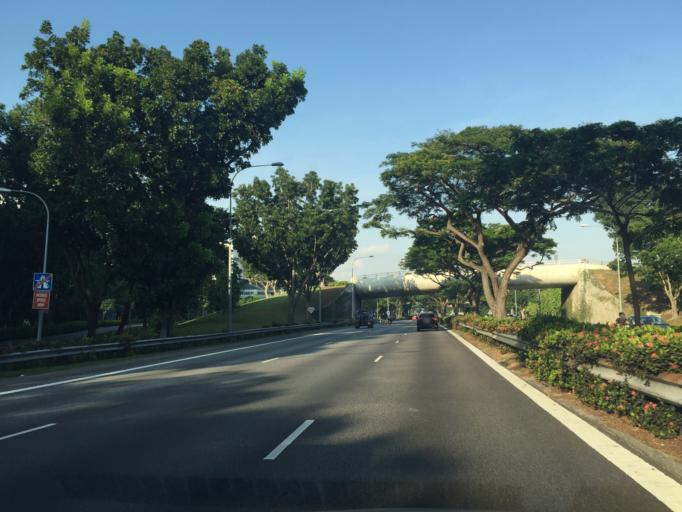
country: SG
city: Singapore
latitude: 1.3434
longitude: 103.9491
